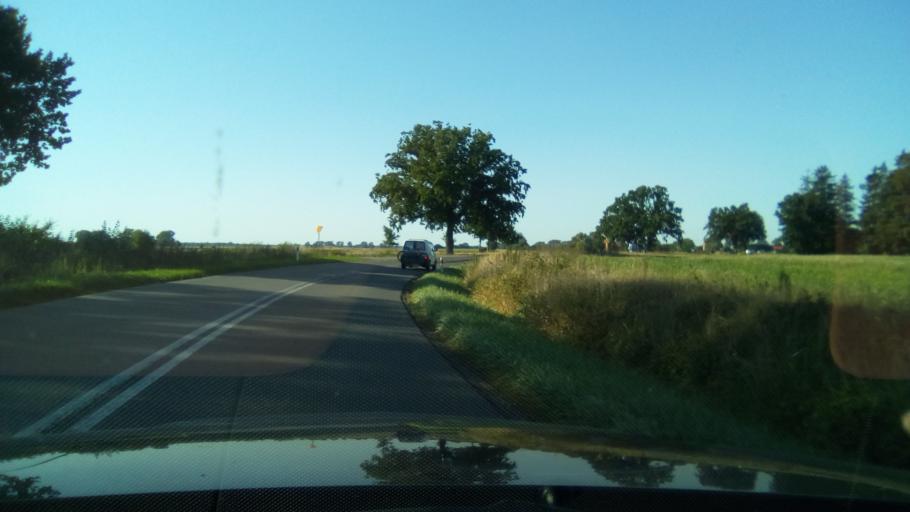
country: PL
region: West Pomeranian Voivodeship
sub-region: Powiat kamienski
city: Golczewo
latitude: 53.8245
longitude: 14.9316
